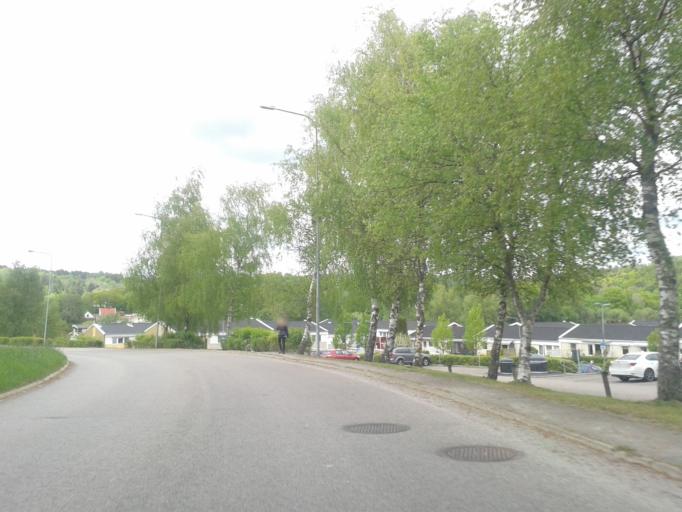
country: SE
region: Vaestra Goetaland
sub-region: Kungalvs Kommun
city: Kungalv
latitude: 57.8782
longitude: 11.9939
